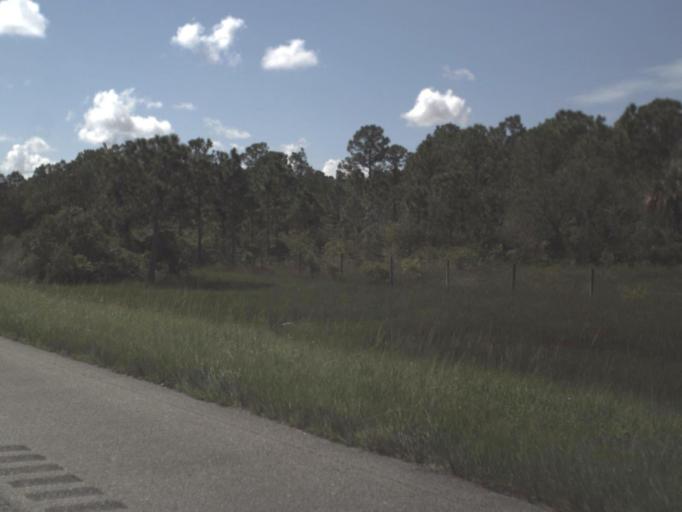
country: US
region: Florida
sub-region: Lee County
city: Suncoast Estates
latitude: 26.7932
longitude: -81.9087
